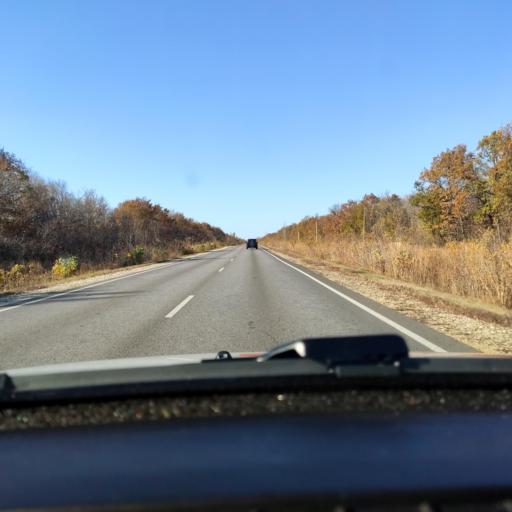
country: RU
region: Voronezj
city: Zemlyansk
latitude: 51.8291
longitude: 38.8283
